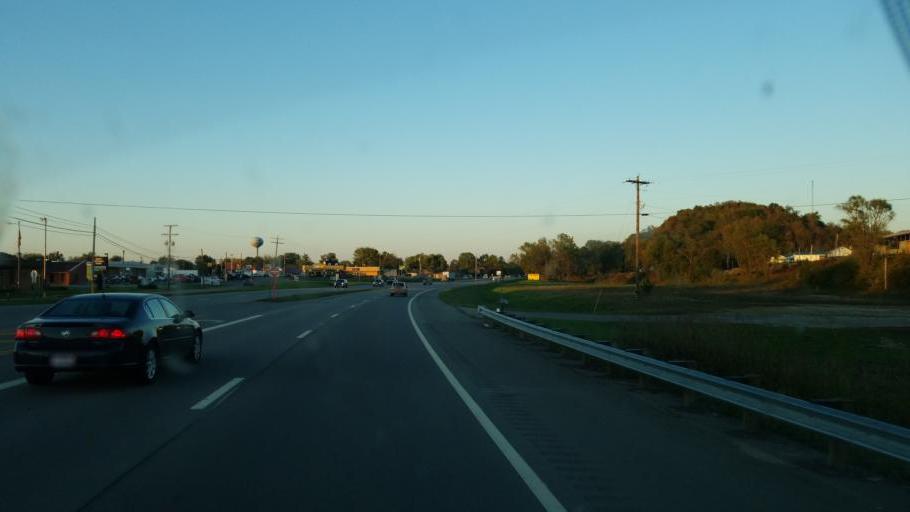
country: US
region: Ohio
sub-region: Pike County
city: Piketon
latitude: 39.0606
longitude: -83.0178
